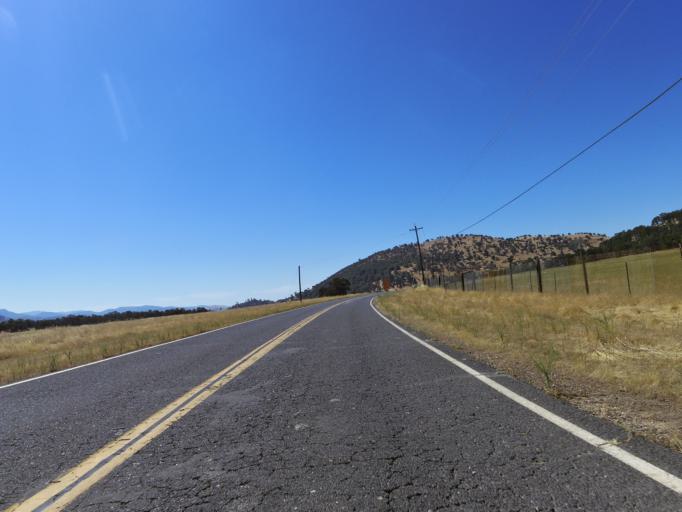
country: US
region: California
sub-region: Tuolumne County
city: Tuolumne City
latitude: 37.6407
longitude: -120.3078
